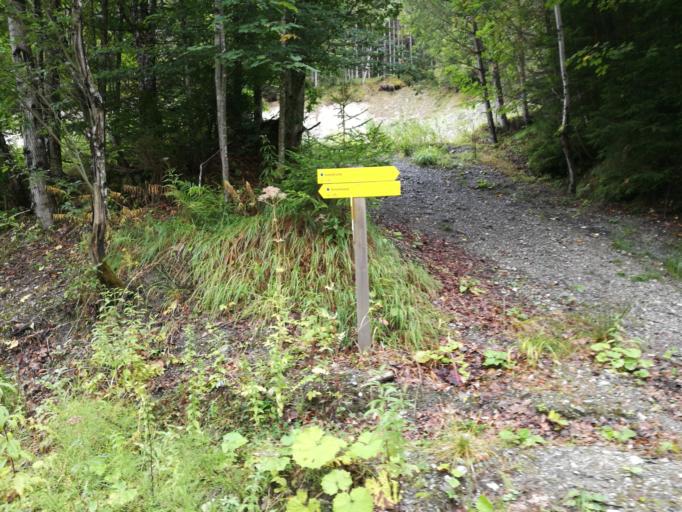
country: AT
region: Salzburg
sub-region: Politischer Bezirk Sankt Johann im Pongau
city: Forstau
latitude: 47.3835
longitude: 13.5421
